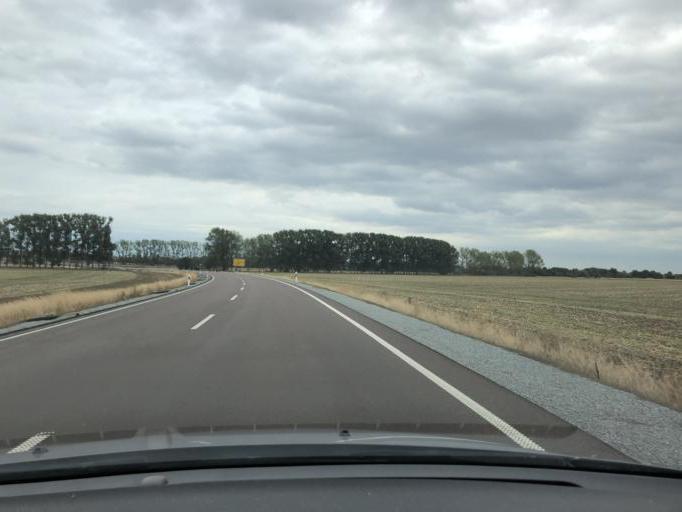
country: DE
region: Saxony-Anhalt
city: Brumby
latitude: 51.8889
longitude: 11.7080
